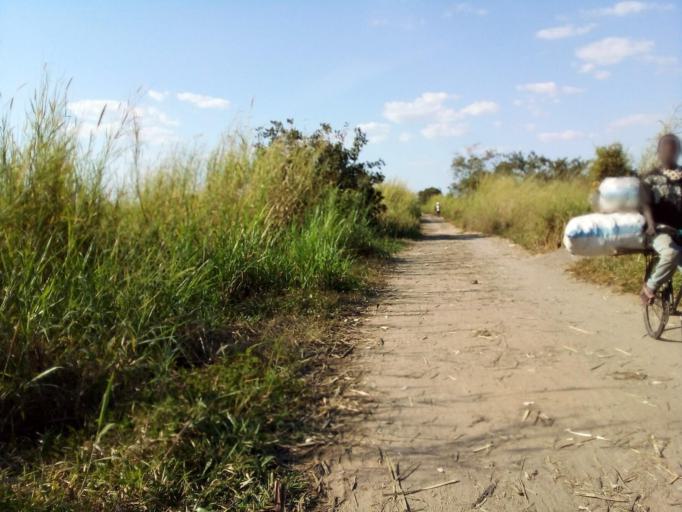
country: MZ
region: Zambezia
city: Quelimane
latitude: -17.5843
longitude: 36.8428
